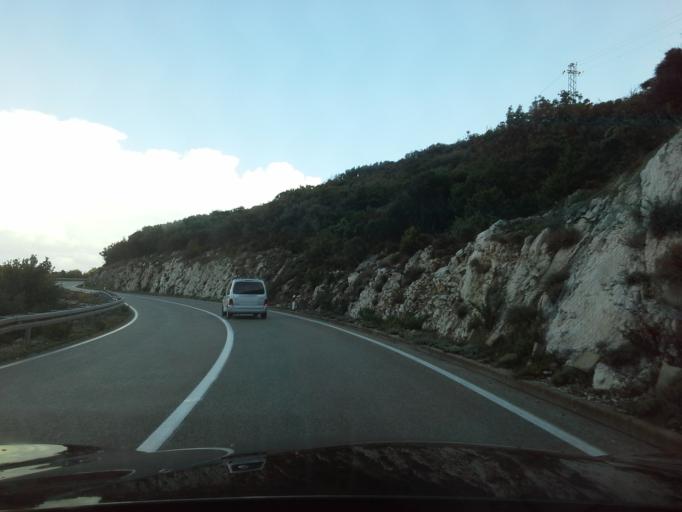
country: HR
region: Primorsko-Goranska
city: Mali Losinj
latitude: 44.6071
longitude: 14.4027
